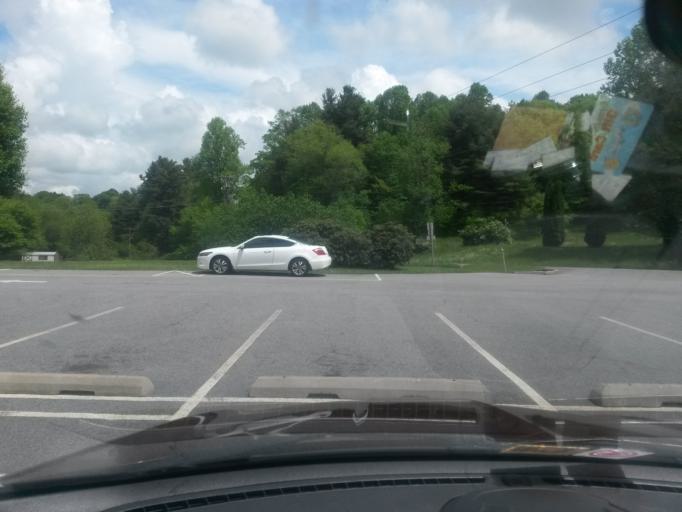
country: US
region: Virginia
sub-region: Patrick County
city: Stuart
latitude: 36.7385
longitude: -80.3900
